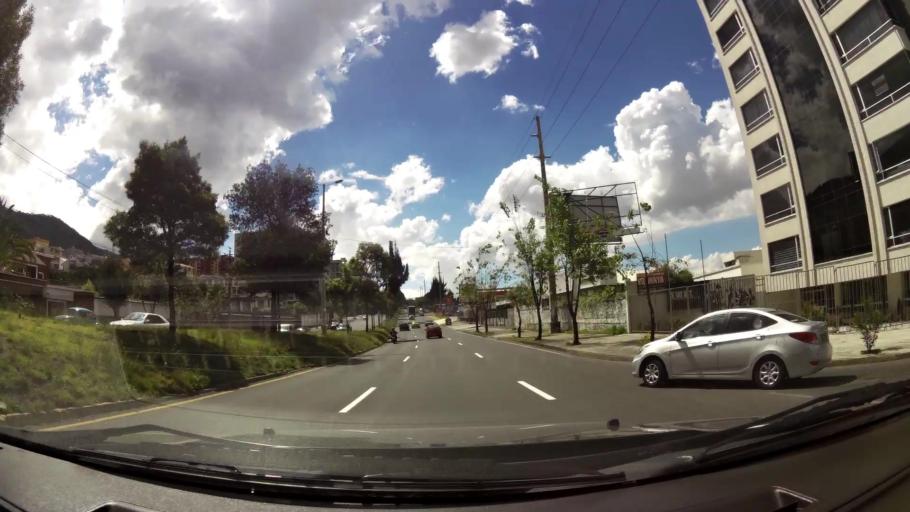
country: EC
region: Pichincha
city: Quito
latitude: -0.1558
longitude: -78.4969
